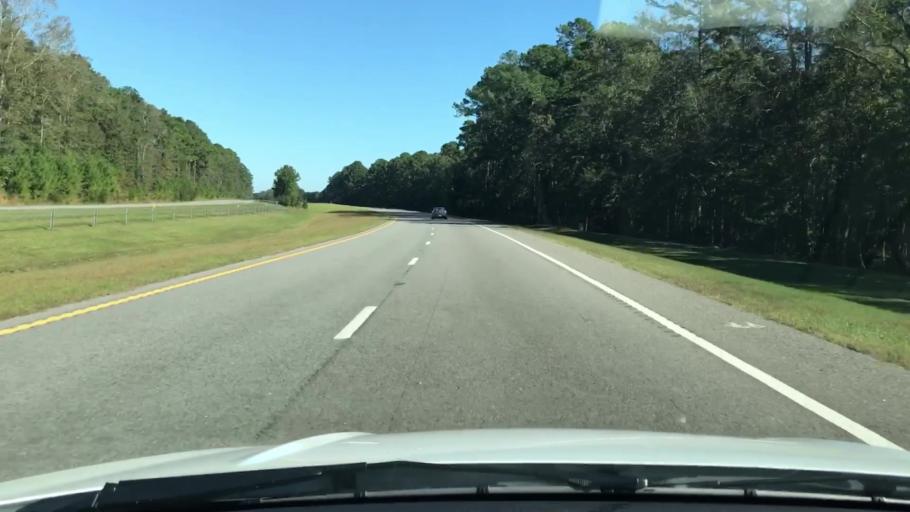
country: US
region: South Carolina
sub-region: Colleton County
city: Walterboro
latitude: 32.7367
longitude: -80.5822
